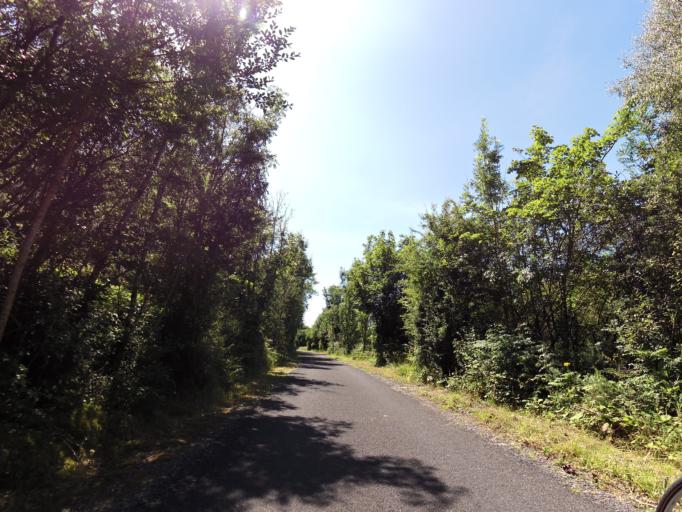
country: IE
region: Munster
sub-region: Waterford
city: Portlaw
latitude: 52.2302
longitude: -7.3139
